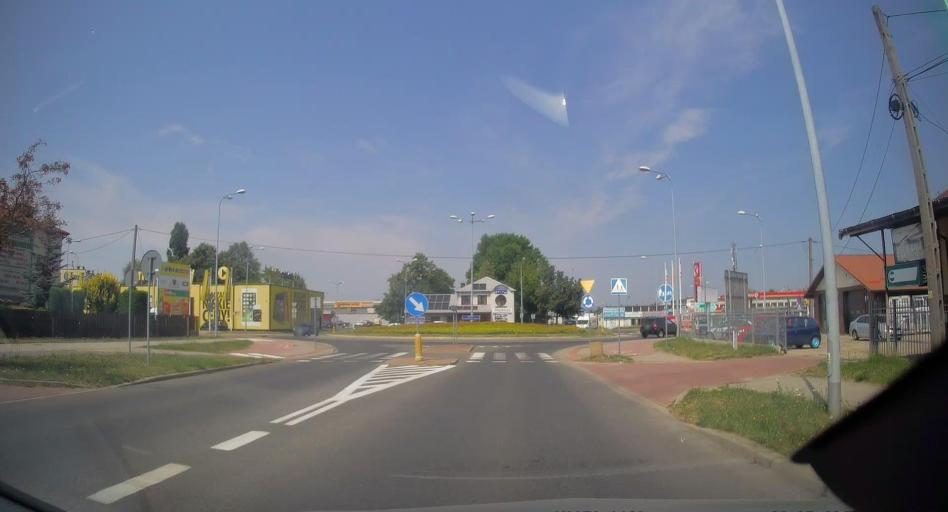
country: PL
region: Subcarpathian Voivodeship
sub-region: Powiat debicki
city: Debica
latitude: 50.0539
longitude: 21.4317
